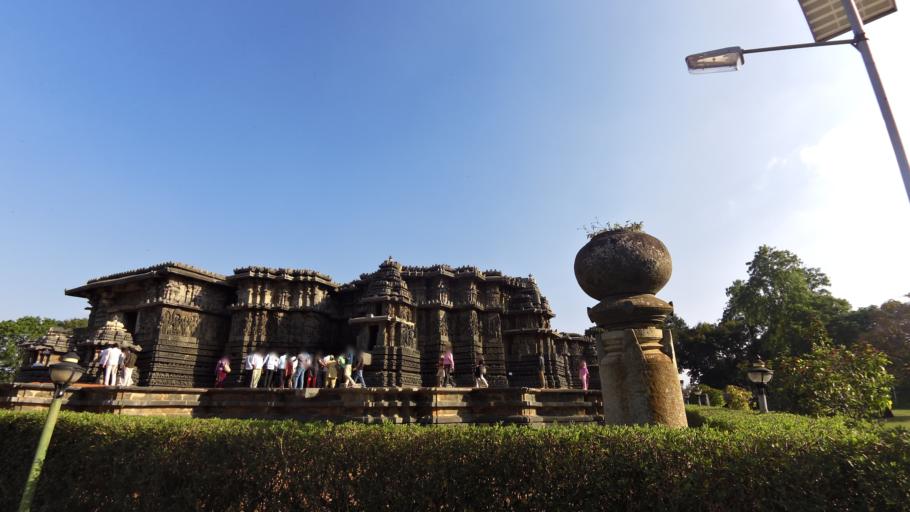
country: IN
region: Karnataka
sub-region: Hassan
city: Belur
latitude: 13.2129
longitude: 75.9939
